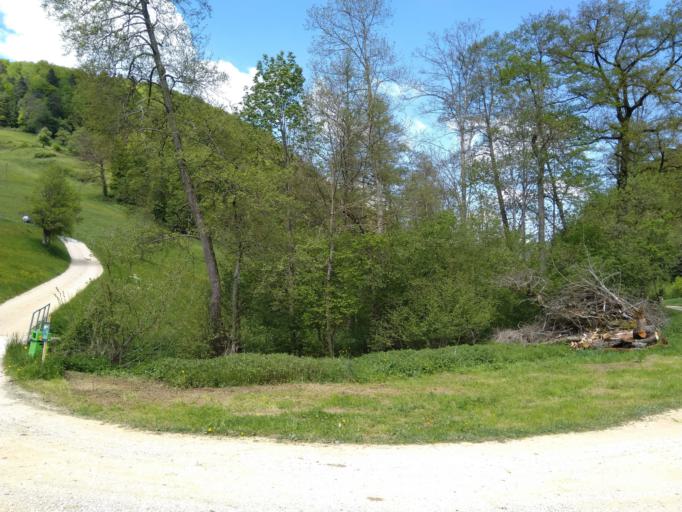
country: CH
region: Basel-Landschaft
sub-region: Bezirk Laufen
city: Wahlen
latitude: 47.3846
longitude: 7.4842
